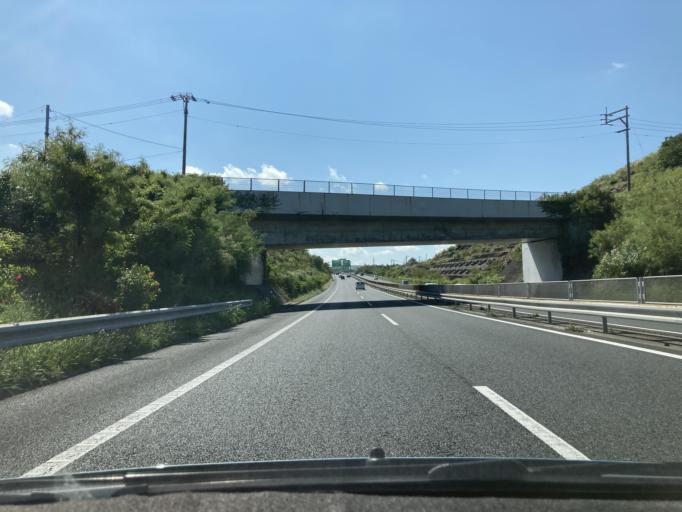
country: JP
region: Okinawa
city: Ginowan
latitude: 26.2350
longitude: 127.7403
